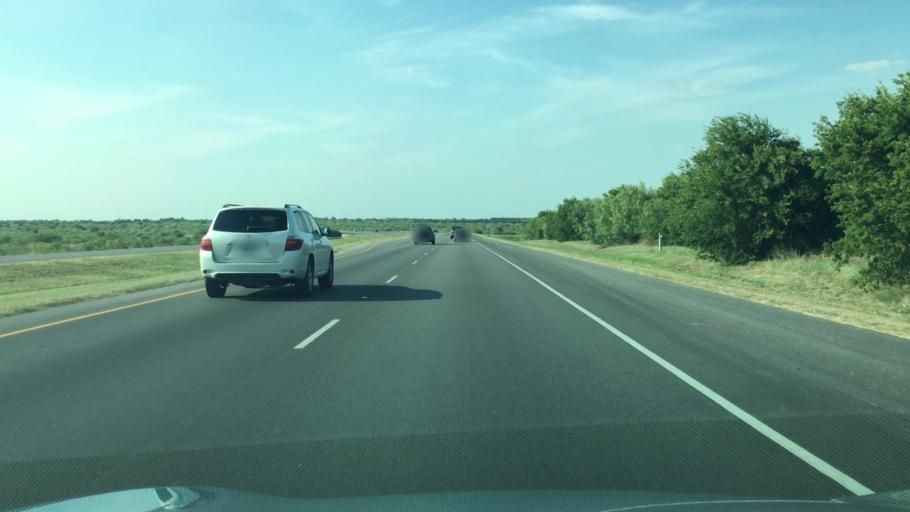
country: US
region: Texas
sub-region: Hays County
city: Kyle
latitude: 30.0323
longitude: -97.8723
